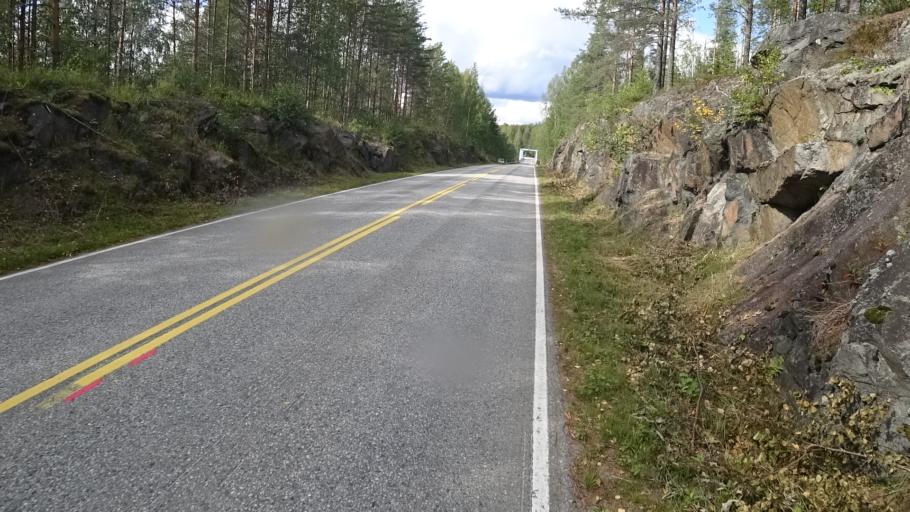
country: FI
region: North Karelia
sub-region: Joensuu
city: Ilomantsi
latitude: 62.6197
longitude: 31.2014
